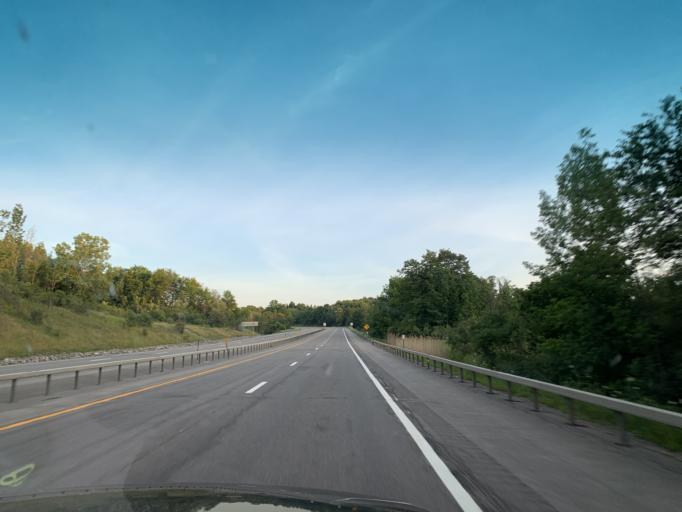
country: US
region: New York
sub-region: Oneida County
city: Chadwicks
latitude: 43.0372
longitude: -75.2714
